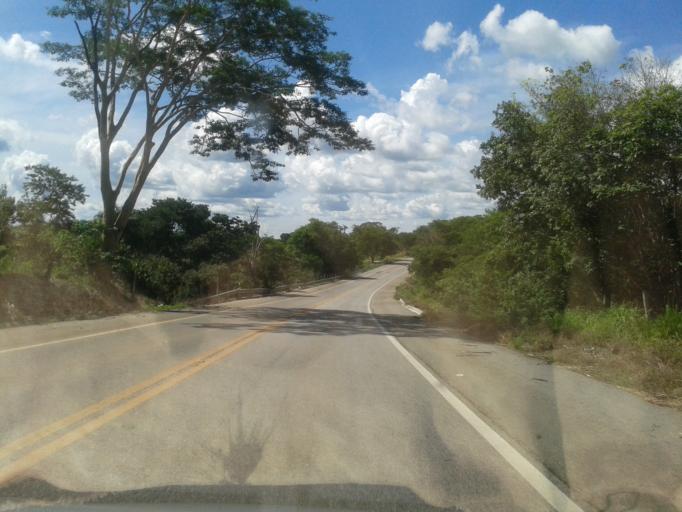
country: BR
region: Goias
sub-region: Itapuranga
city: Itapuranga
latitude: -15.6565
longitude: -50.2215
